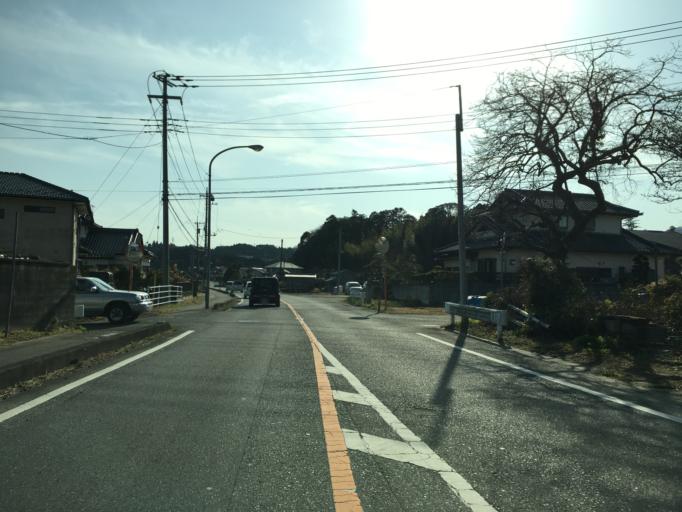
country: JP
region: Ibaraki
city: Takahagi
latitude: 36.7403
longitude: 140.6901
